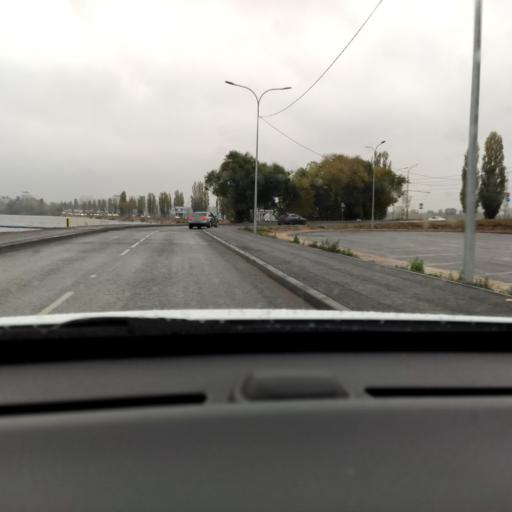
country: RU
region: Voronezj
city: Voronezh
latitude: 51.6681
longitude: 39.2282
